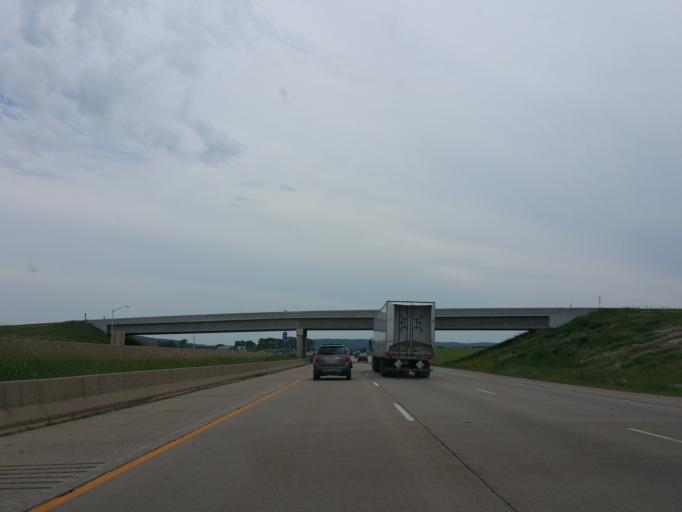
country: US
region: Wisconsin
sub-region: Columbia County
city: Poynette
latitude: 43.4221
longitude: -89.4762
